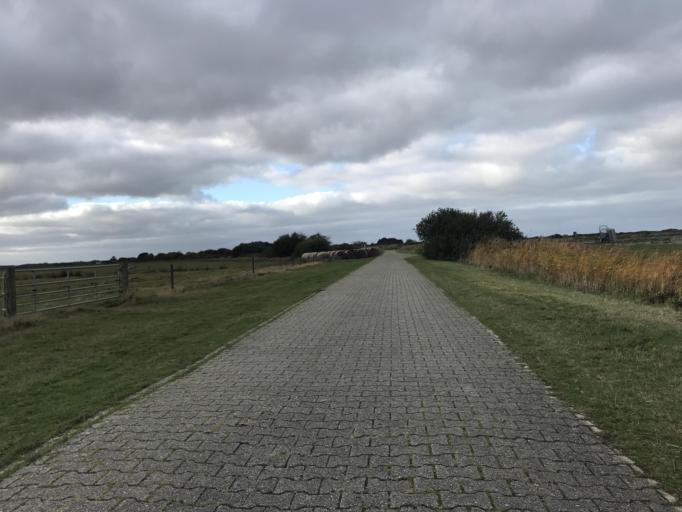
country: DE
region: Lower Saxony
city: Borkum
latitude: 53.5971
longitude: 6.7374
